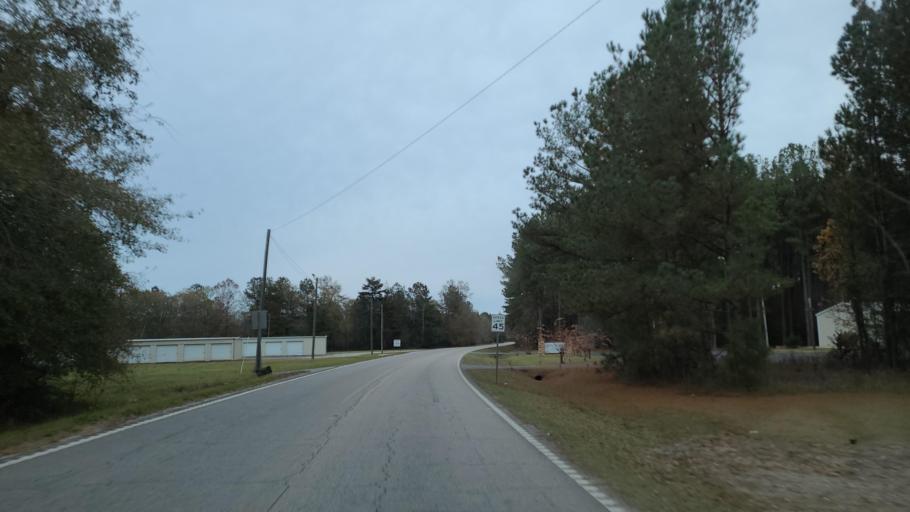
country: US
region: Mississippi
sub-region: Clarke County
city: Stonewall
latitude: 32.0391
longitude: -88.8808
